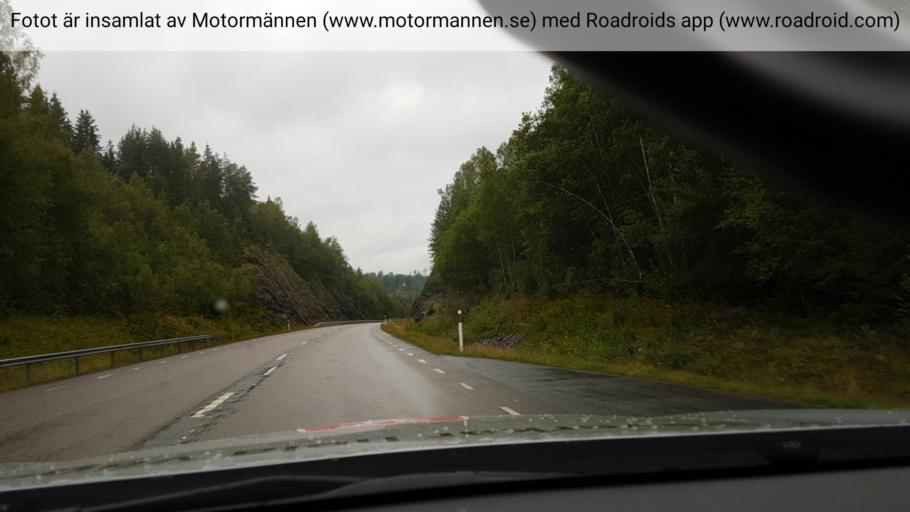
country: SE
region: Vaestra Goetaland
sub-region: Bengtsfors Kommun
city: Billingsfors
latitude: 58.9275
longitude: 12.1491
